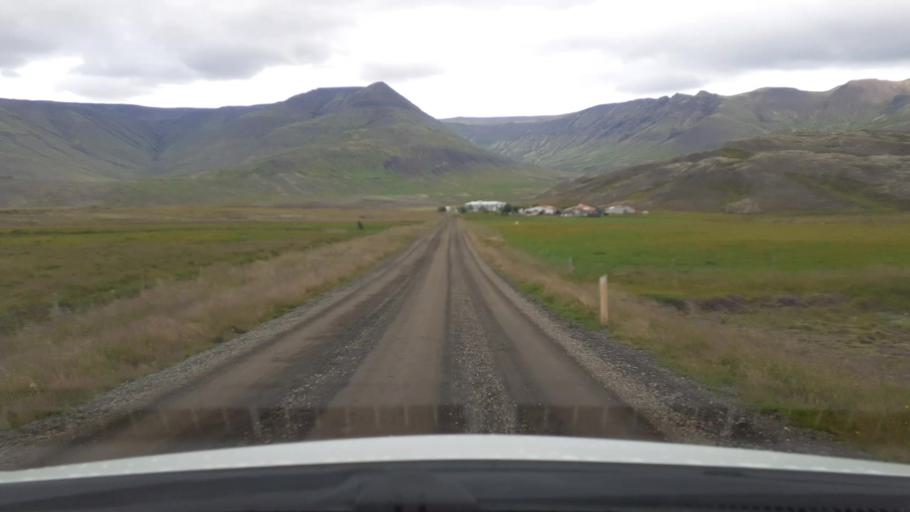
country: IS
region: Capital Region
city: Mosfellsbaer
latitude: 64.2004
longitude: -21.5586
